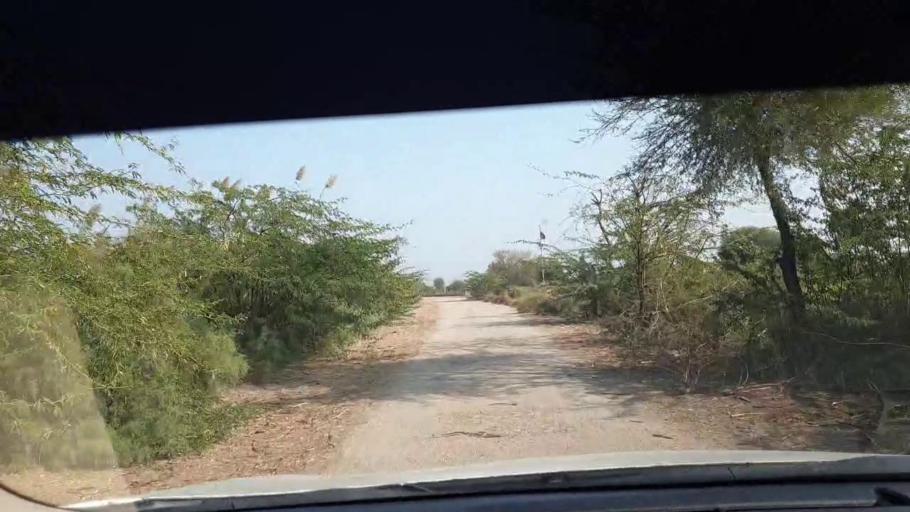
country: PK
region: Sindh
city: Berani
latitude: 25.8232
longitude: 68.7644
